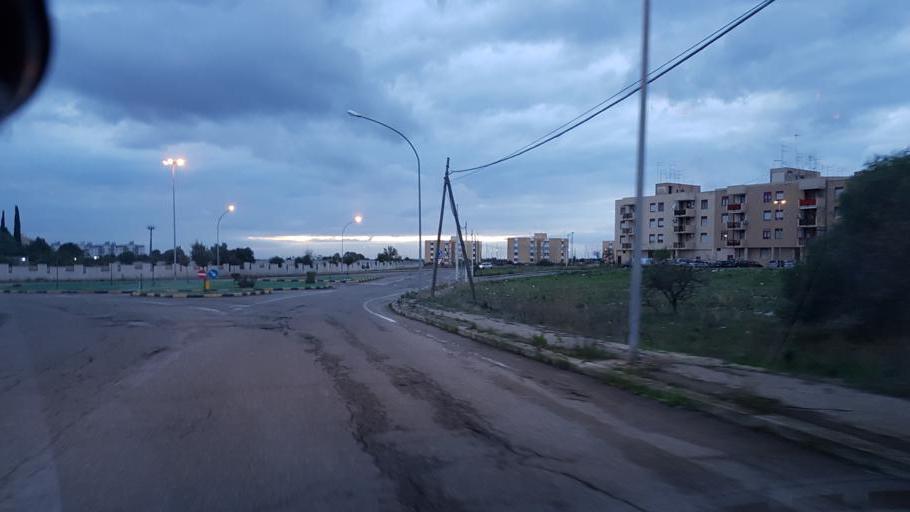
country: IT
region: Apulia
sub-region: Provincia di Taranto
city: Paolo VI
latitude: 40.5313
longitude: 17.2823
